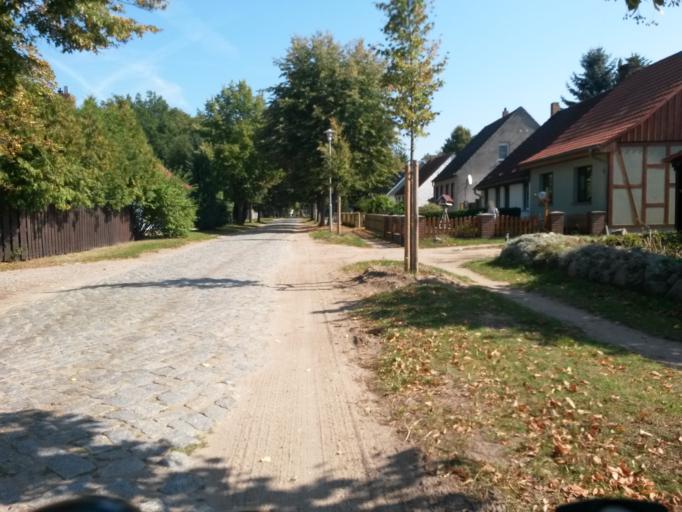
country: DE
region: Brandenburg
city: Templin
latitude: 53.0495
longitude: 13.5278
